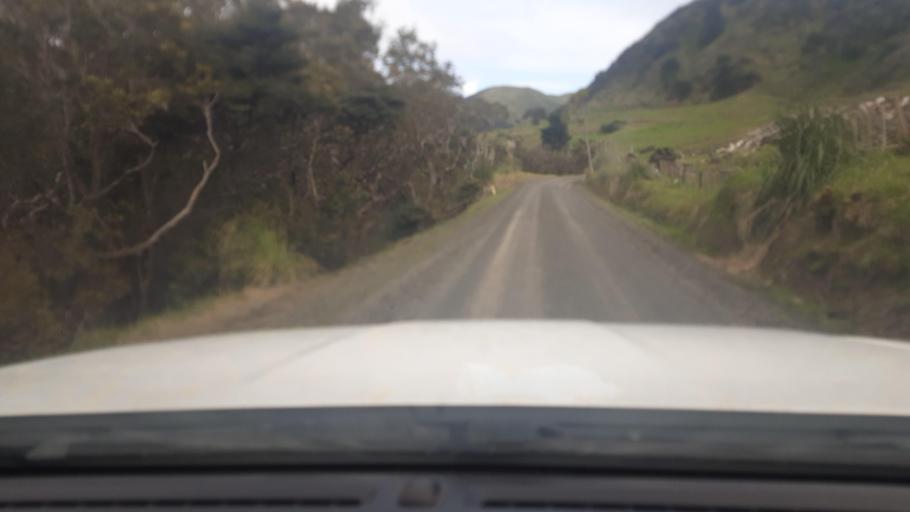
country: NZ
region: Northland
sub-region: Far North District
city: Ahipara
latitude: -35.3341
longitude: 173.2251
